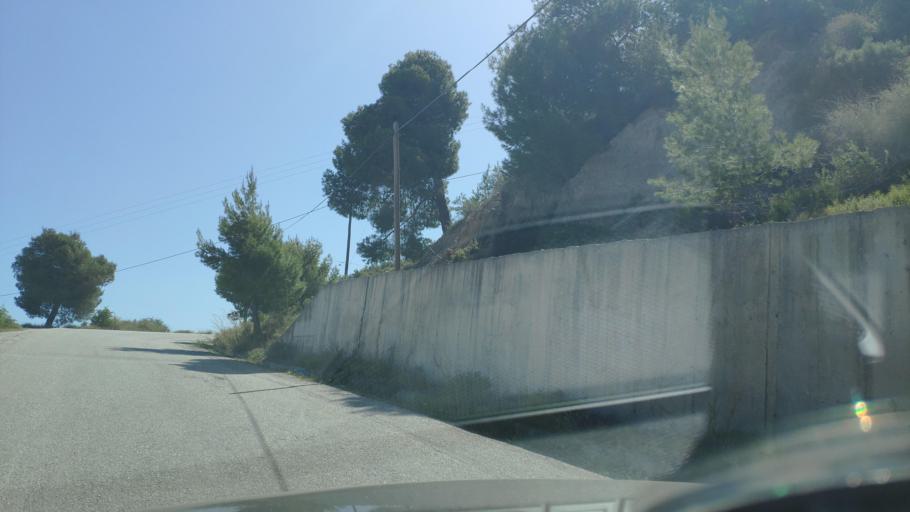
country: GR
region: West Greece
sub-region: Nomos Achaias
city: Aiyira
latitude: 38.1288
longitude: 22.3444
